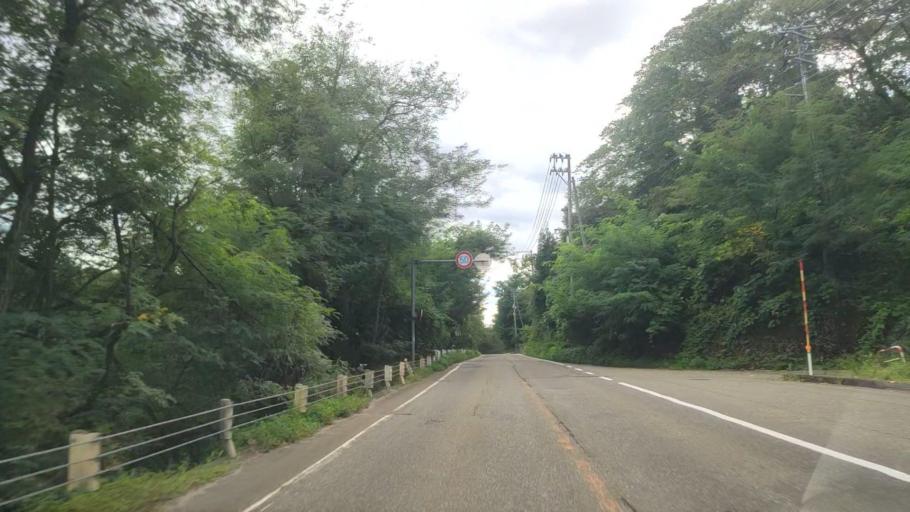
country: JP
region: Niigata
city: Arai
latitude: 36.9975
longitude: 138.2674
